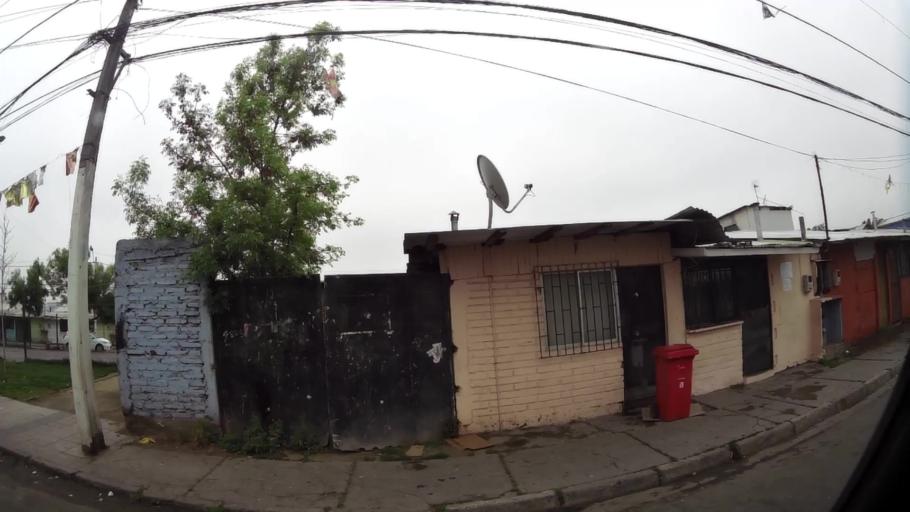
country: CL
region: Santiago Metropolitan
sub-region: Provincia de Santiago
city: Santiago
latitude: -33.4854
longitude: -70.6384
